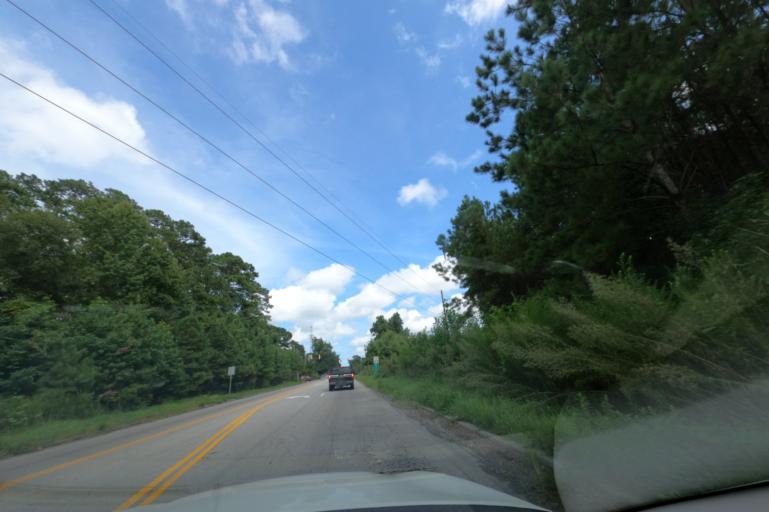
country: US
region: South Carolina
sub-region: Charleston County
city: Shell Point
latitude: 32.7220
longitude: -80.0873
